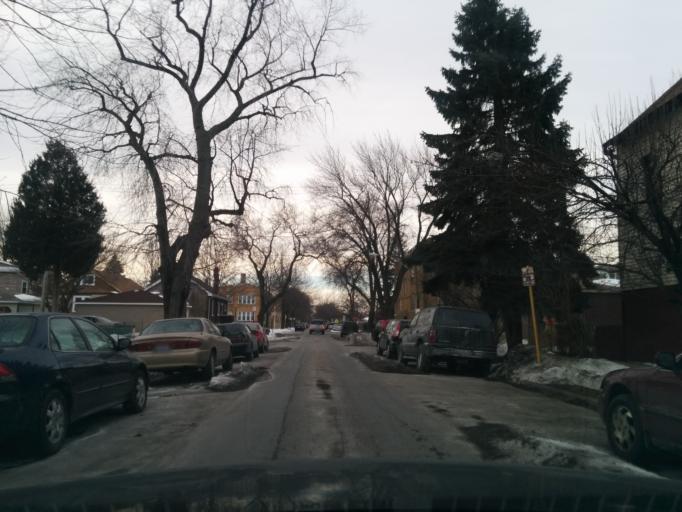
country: US
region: Illinois
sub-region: Cook County
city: Harwood Heights
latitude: 41.9424
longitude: -87.7519
